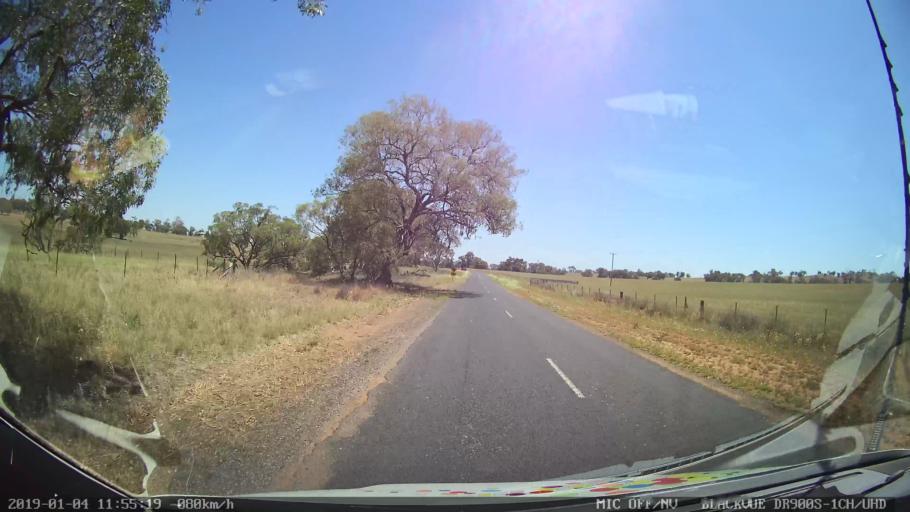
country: AU
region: New South Wales
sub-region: Cabonne
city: Molong
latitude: -32.8553
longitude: 148.7242
